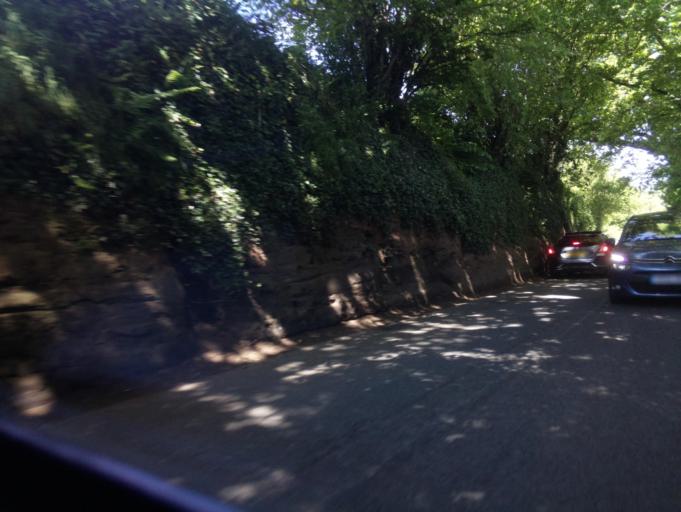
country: GB
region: England
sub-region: Devon
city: Newton Poppleford
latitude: 50.6759
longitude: -3.3100
